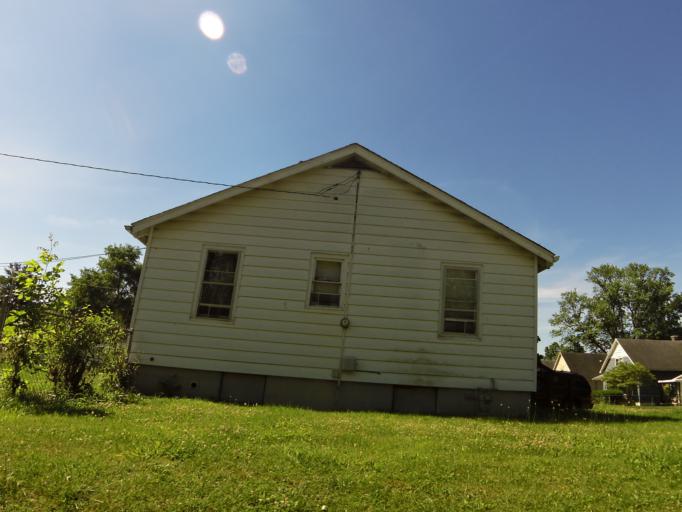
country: US
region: Illinois
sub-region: Vermilion County
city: Danville
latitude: 40.1351
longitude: -87.5820
